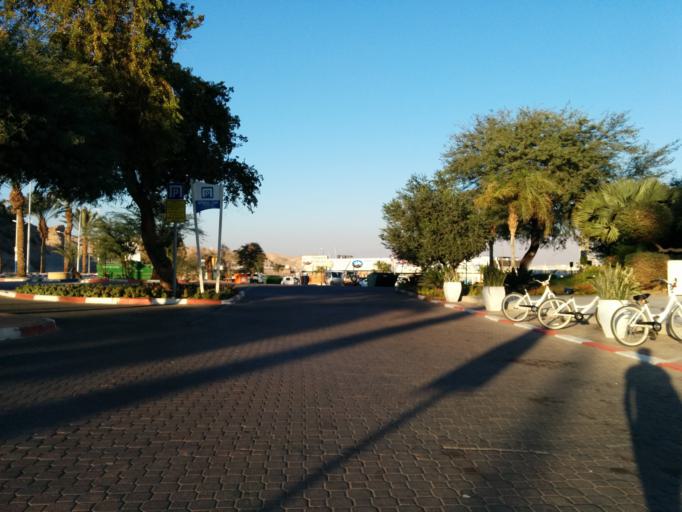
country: IL
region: Southern District
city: Eilat
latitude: 29.5140
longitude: 34.9254
